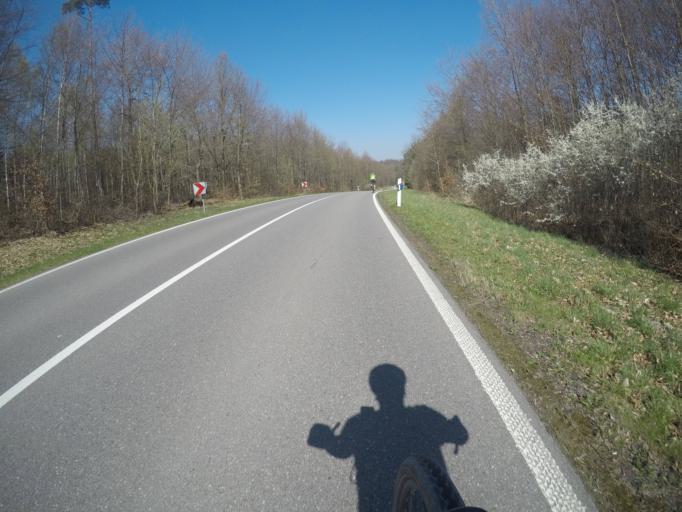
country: DE
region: Baden-Wuerttemberg
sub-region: Regierungsbezirk Stuttgart
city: Leonberg
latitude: 48.7574
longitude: 9.0140
